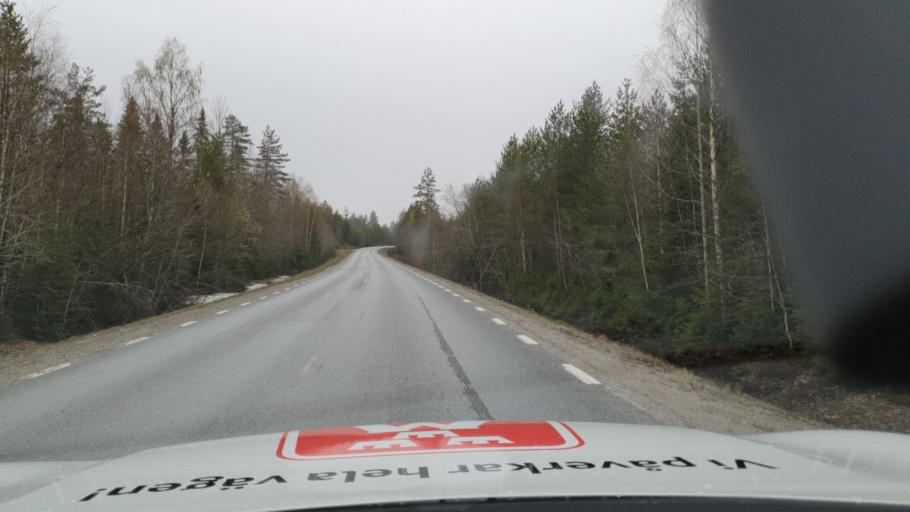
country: SE
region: Vaesterbotten
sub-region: Vannas Kommun
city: Vaennaes
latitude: 63.7831
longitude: 19.7404
